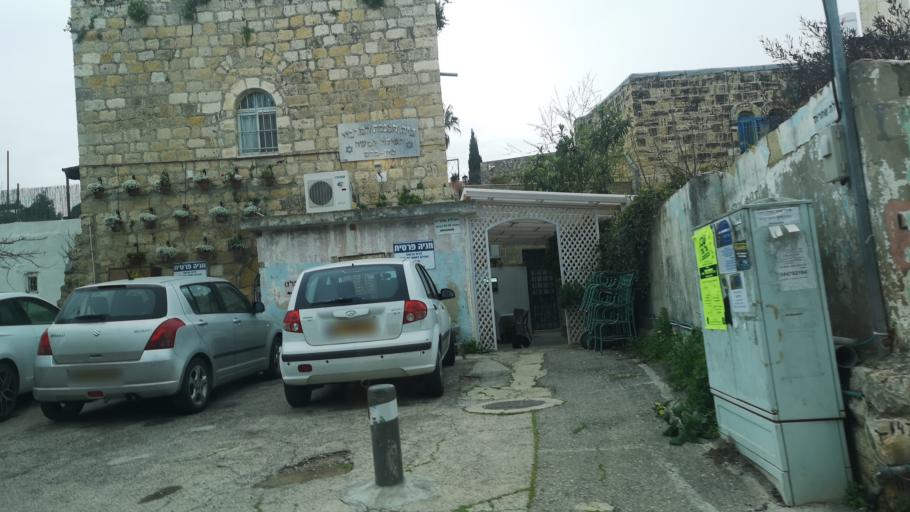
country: PS
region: West Bank
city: Bayt Iksa
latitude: 31.7681
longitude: 35.1621
